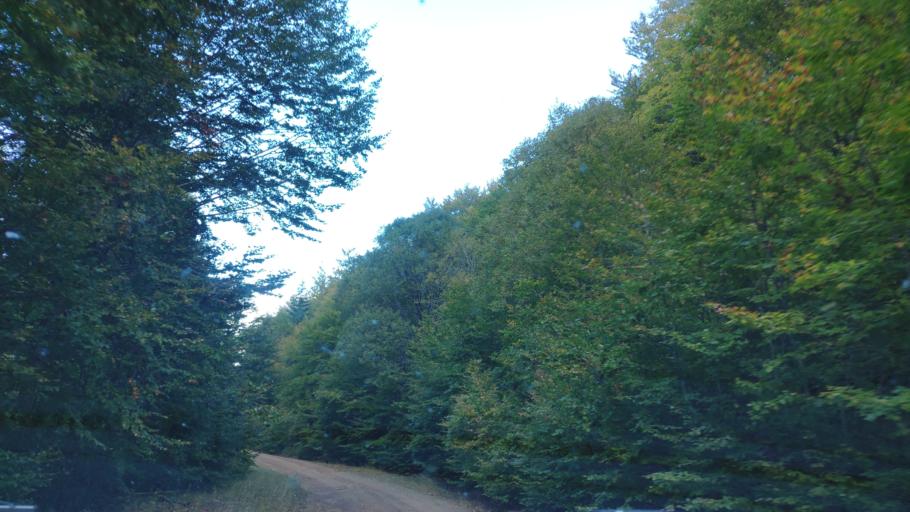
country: GR
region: West Macedonia
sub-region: Nomos Kastorias
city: Nestorio
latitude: 40.3260
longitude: 20.9030
